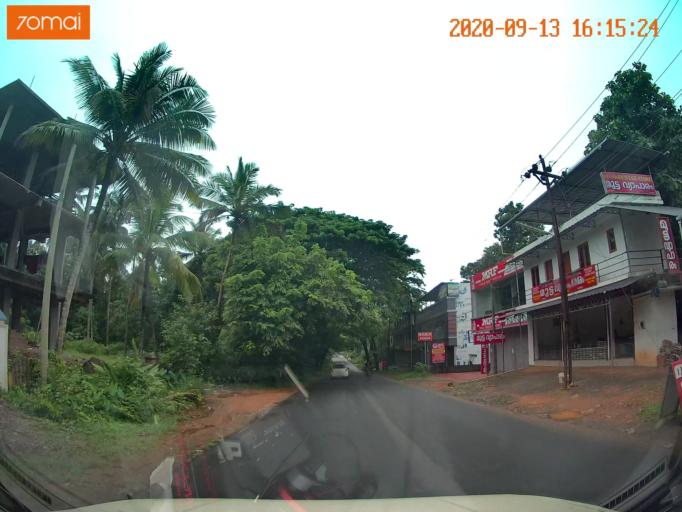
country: IN
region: Kerala
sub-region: Kottayam
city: Palackattumala
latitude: 9.6924
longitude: 76.6419
